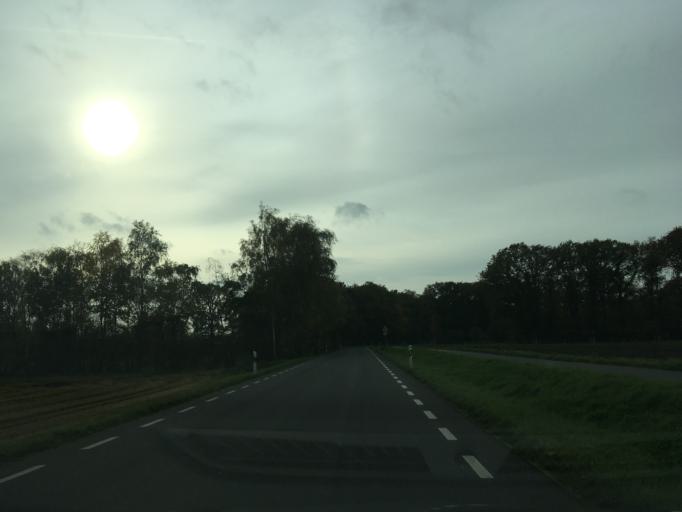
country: DE
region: North Rhine-Westphalia
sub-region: Regierungsbezirk Munster
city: Vreden
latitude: 52.0487
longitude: 6.8608
